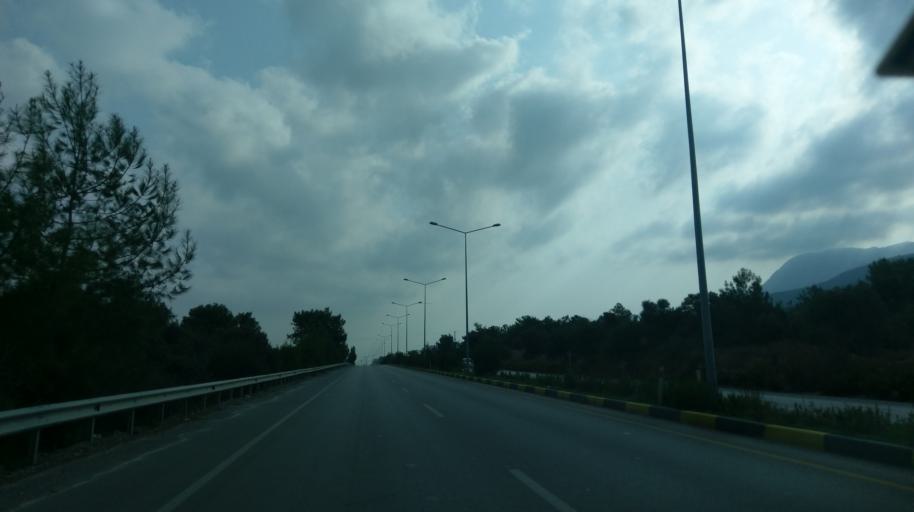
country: CY
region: Keryneia
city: Kyrenia
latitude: 35.3284
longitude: 33.2909
